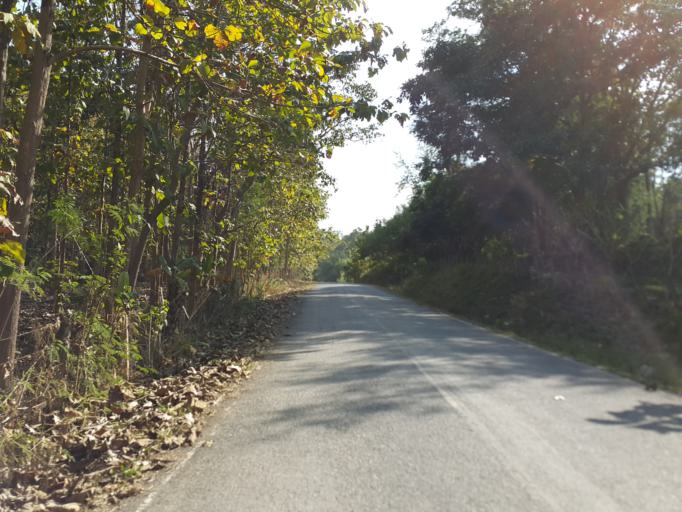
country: TH
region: Chiang Mai
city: Mae On
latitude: 18.7974
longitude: 99.2314
